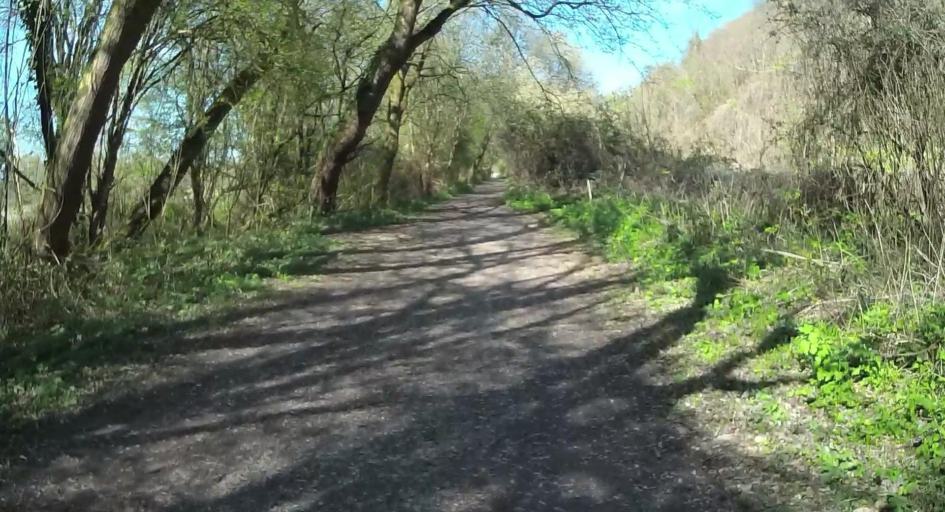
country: GB
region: England
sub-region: Hampshire
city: Romsey
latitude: 51.0806
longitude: -1.5020
